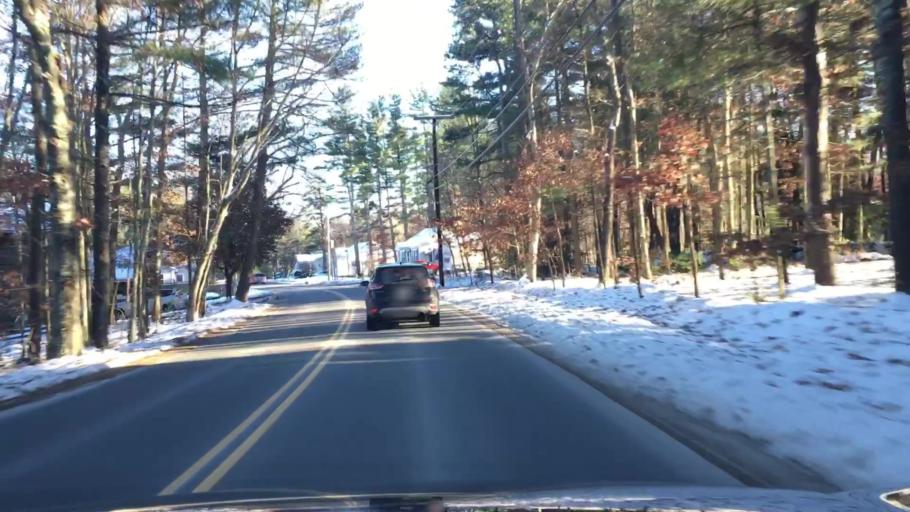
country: US
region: New Hampshire
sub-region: Hillsborough County
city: Milford
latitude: 42.8191
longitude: -71.5798
